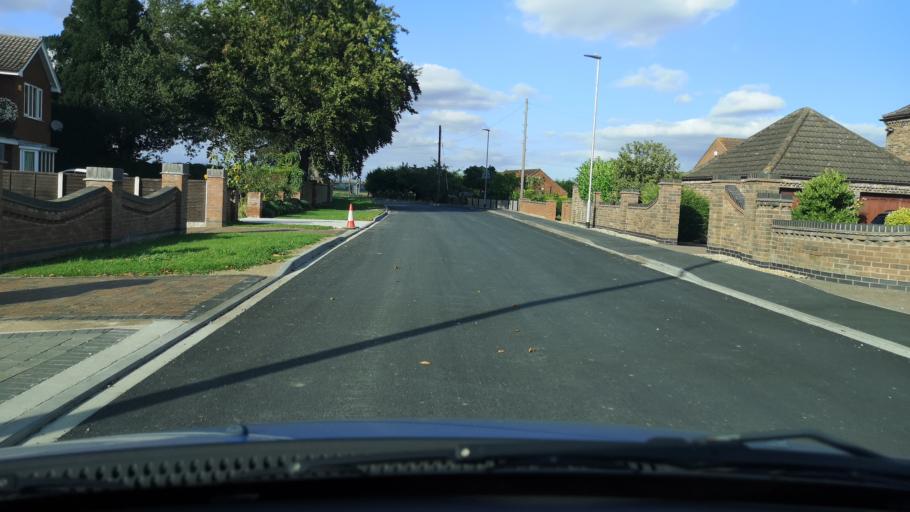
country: GB
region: England
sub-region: North Lincolnshire
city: Gunness
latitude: 53.5788
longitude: -0.7391
